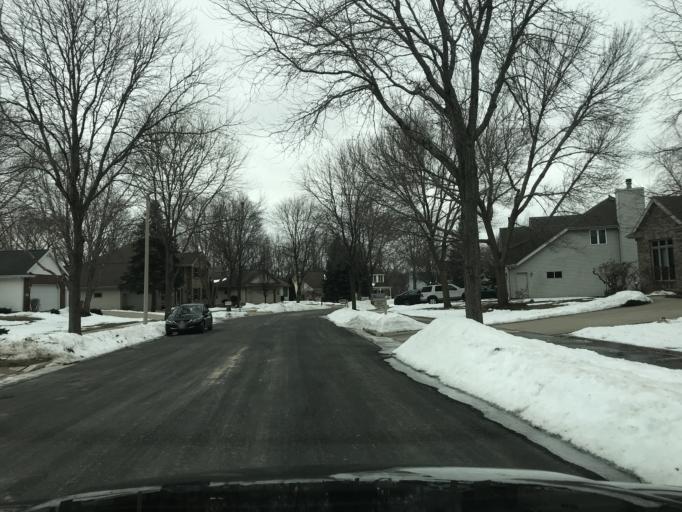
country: US
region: Wisconsin
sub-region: Dane County
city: Monona
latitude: 43.0837
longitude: -89.2725
